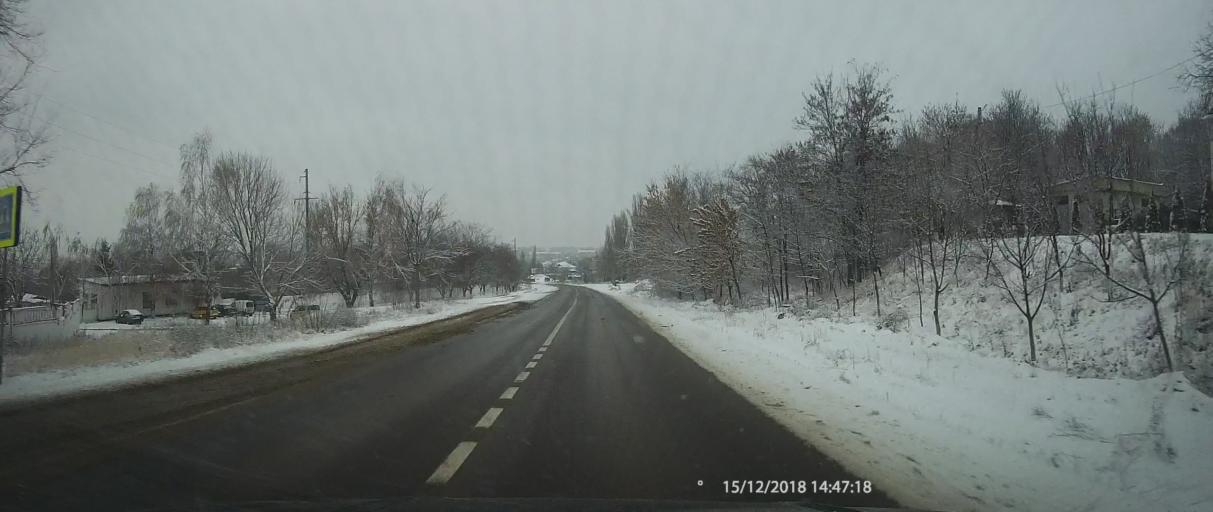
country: MD
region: Cahul
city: Cahul
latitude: 45.8920
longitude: 28.2076
